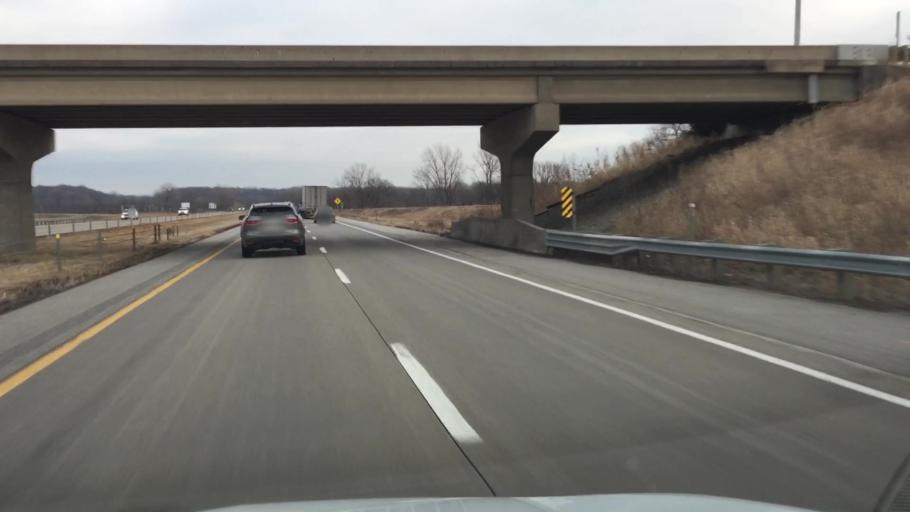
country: US
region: Iowa
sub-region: Jasper County
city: Colfax
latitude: 41.6906
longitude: -93.1803
